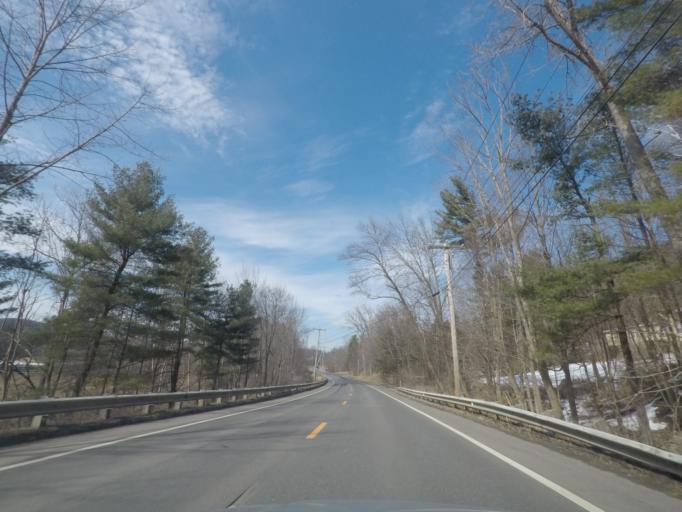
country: US
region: Massachusetts
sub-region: Berkshire County
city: West Stockbridge
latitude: 42.3227
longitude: -73.3587
